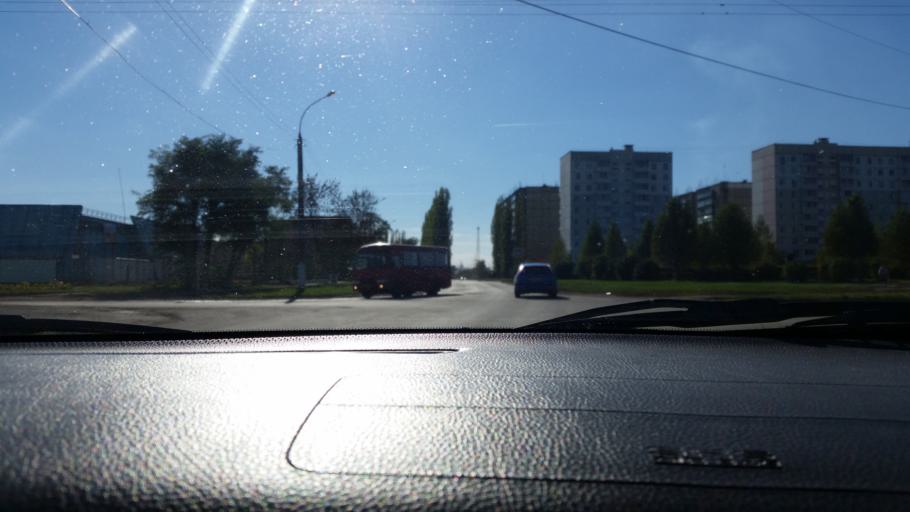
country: RU
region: Lipetsk
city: Gryazi
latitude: 52.4757
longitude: 39.9478
